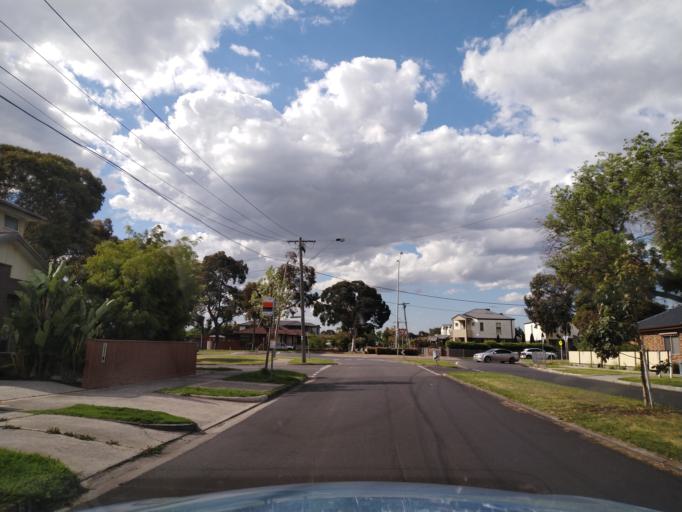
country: AU
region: Victoria
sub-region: Hobsons Bay
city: South Kingsville
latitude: -37.8411
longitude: 144.8643
